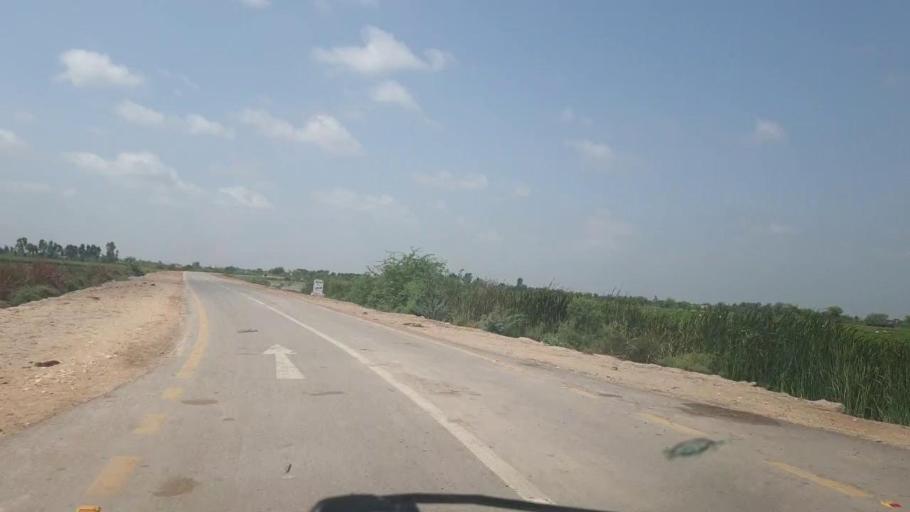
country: PK
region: Sindh
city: Berani
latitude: 25.6910
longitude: 68.9293
